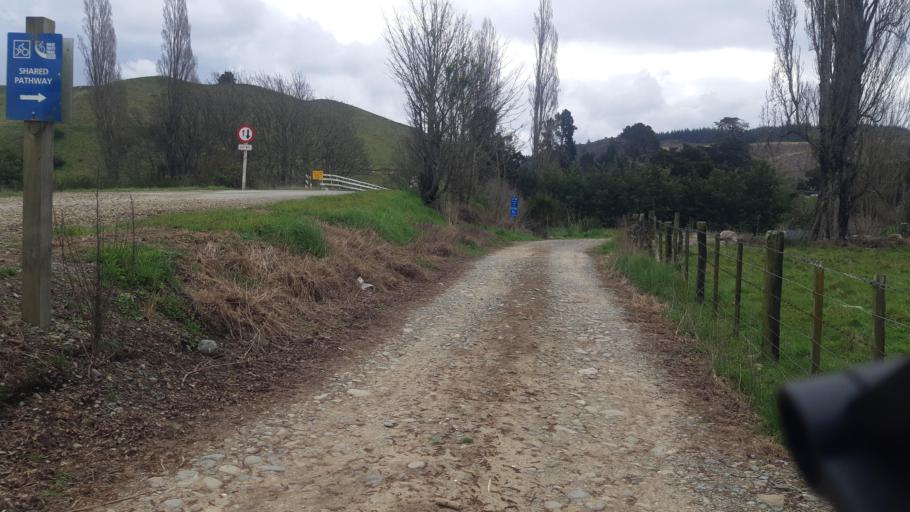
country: NZ
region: Tasman
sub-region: Tasman District
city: Wakefield
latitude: -41.4165
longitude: 173.0041
